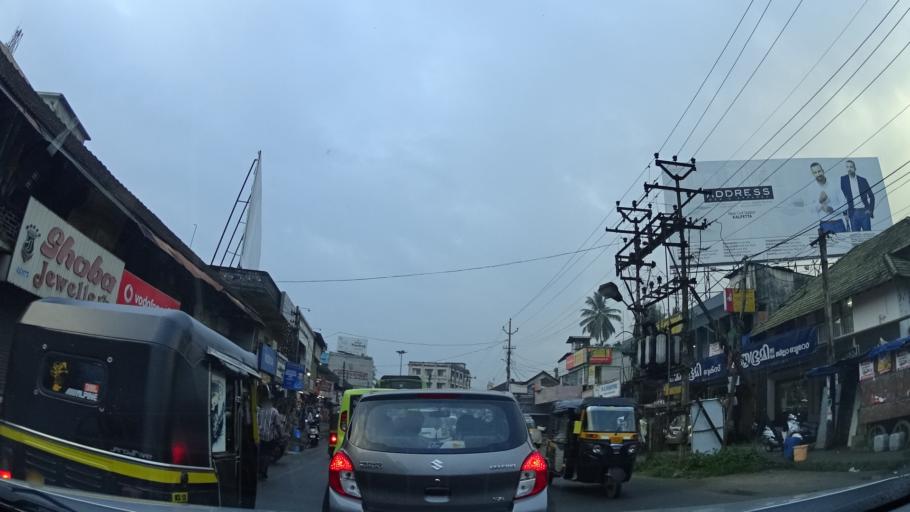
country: IN
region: Kerala
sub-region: Wayanad
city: Kalpetta
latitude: 11.6096
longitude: 76.0832
